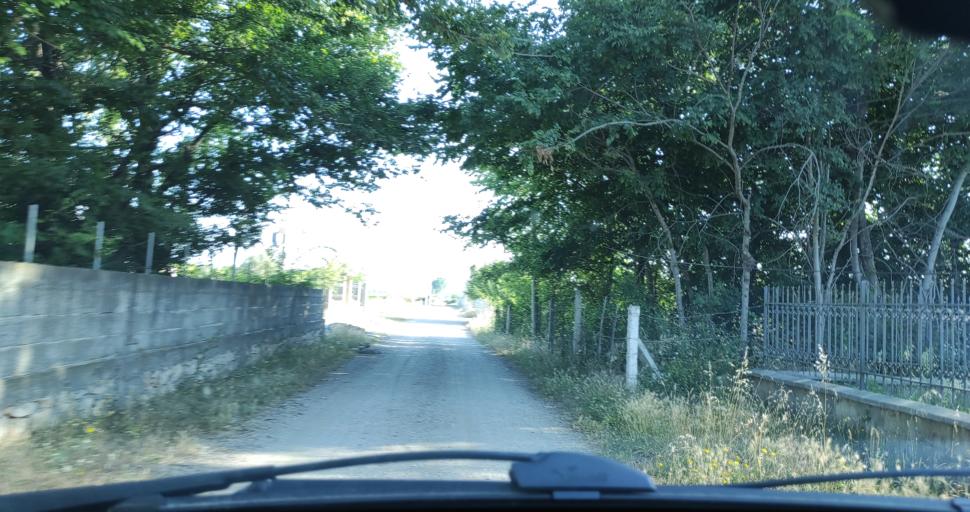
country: AL
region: Shkoder
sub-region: Rrethi i Shkodres
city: Velipoje
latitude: 41.8692
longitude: 19.4261
